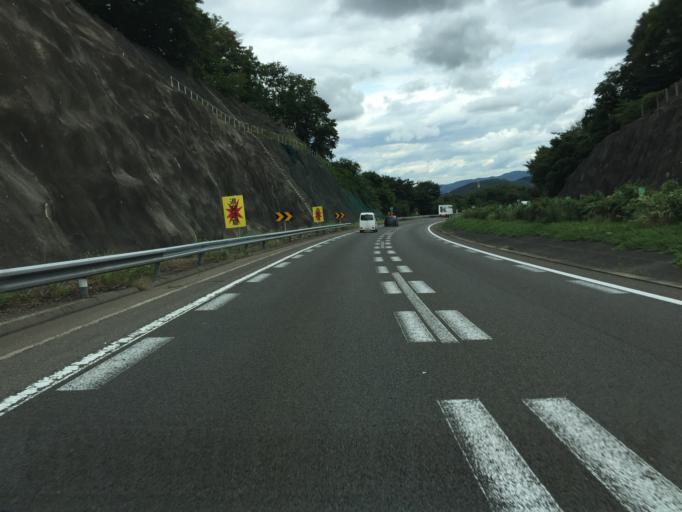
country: JP
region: Miyagi
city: Shiroishi
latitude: 37.9432
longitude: 140.6121
